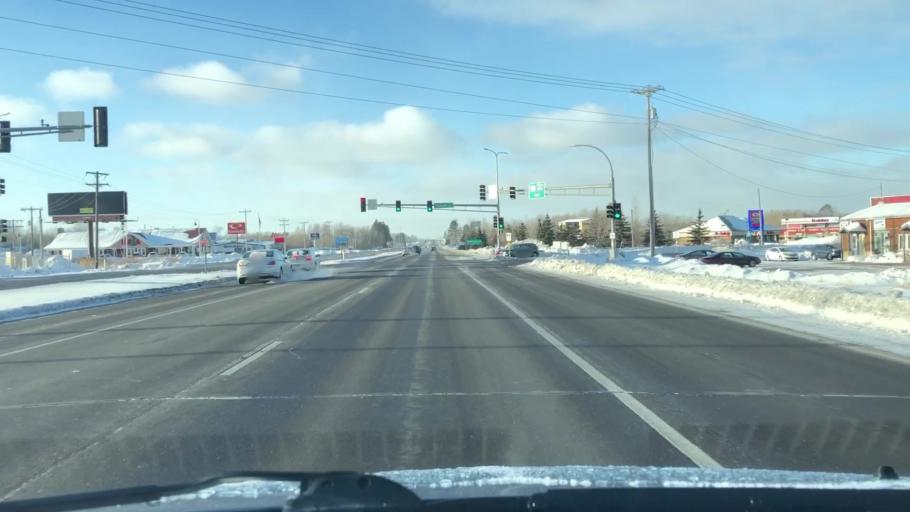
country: US
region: Minnesota
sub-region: Saint Louis County
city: Hermantown
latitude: 46.8145
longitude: -92.1741
